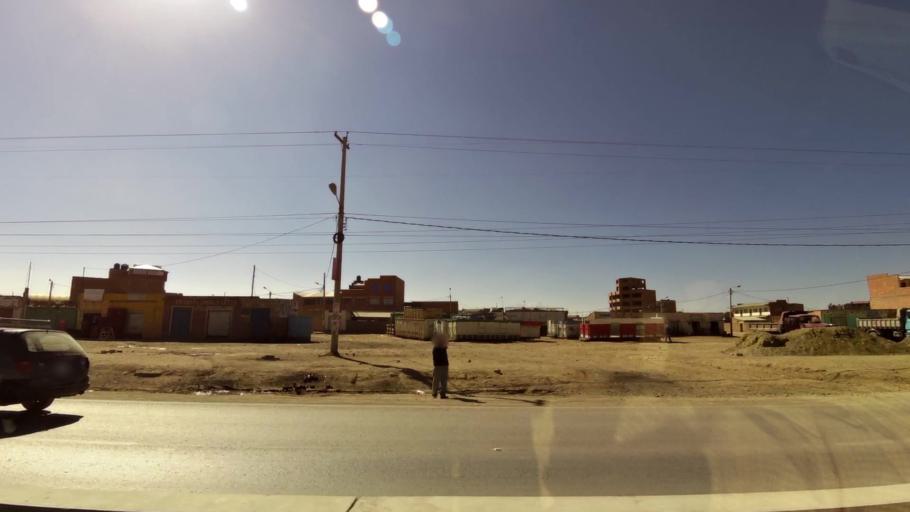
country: BO
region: La Paz
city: La Paz
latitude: -16.6023
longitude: -68.1836
